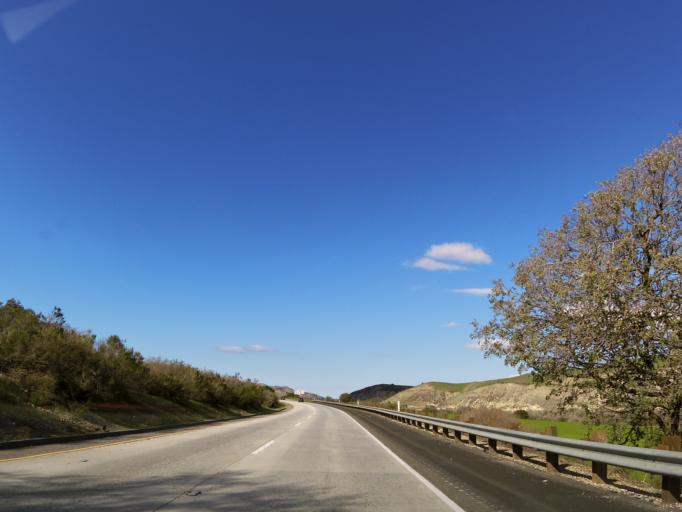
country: US
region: California
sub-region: San Luis Obispo County
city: Lake Nacimiento
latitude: 35.9089
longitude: -120.8468
